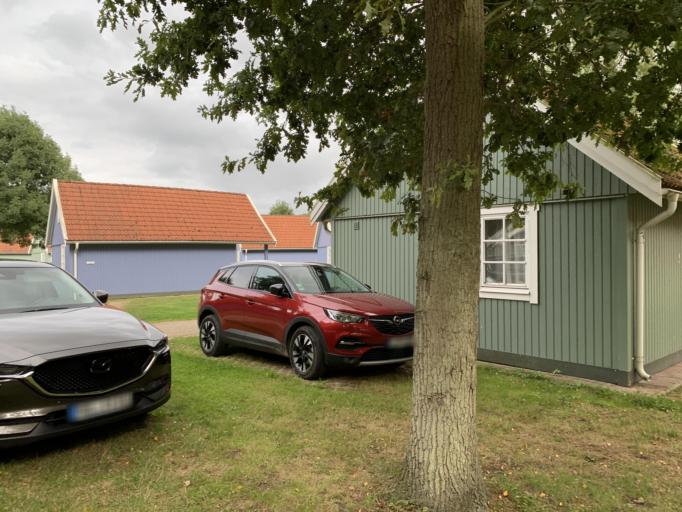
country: DE
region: Mecklenburg-Vorpommern
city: Nienhagen
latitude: 54.1969
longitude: 12.1503
